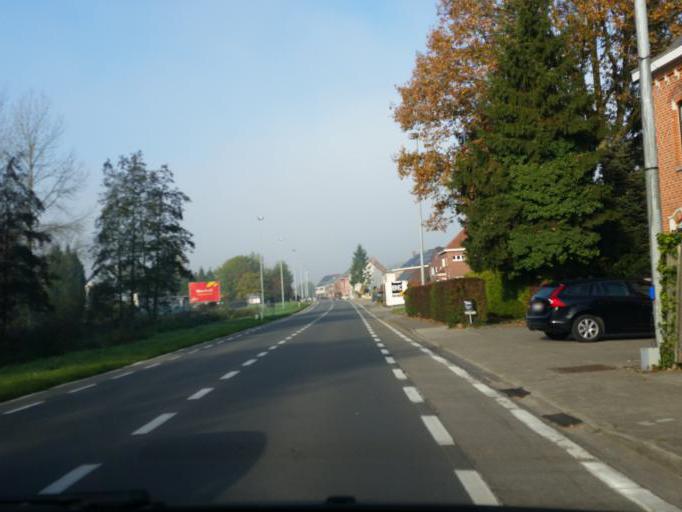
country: BE
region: Flanders
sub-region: Provincie Oost-Vlaanderen
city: Aalst
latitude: 50.9447
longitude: 4.0831
